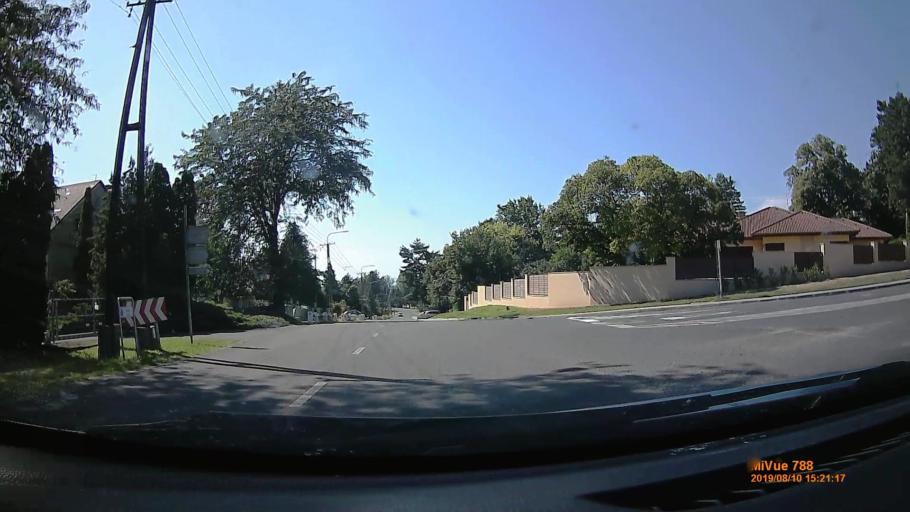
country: HU
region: Somogy
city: Fonyod
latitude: 46.7318
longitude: 17.5400
